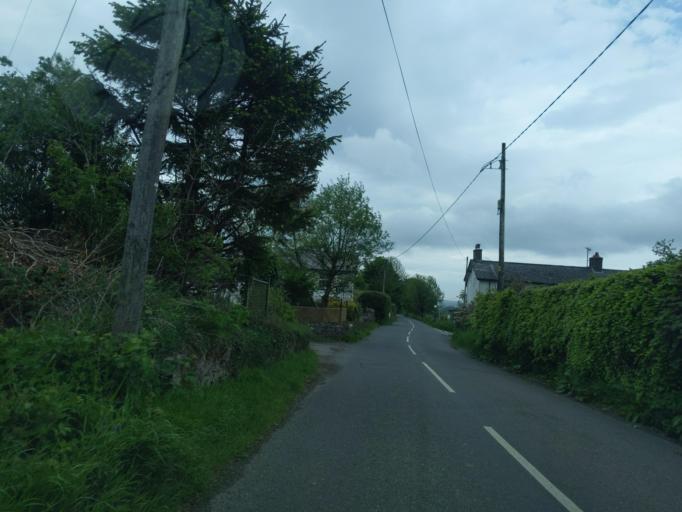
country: GB
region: England
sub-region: Devon
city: Tavistock
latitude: 50.6104
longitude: -4.1580
